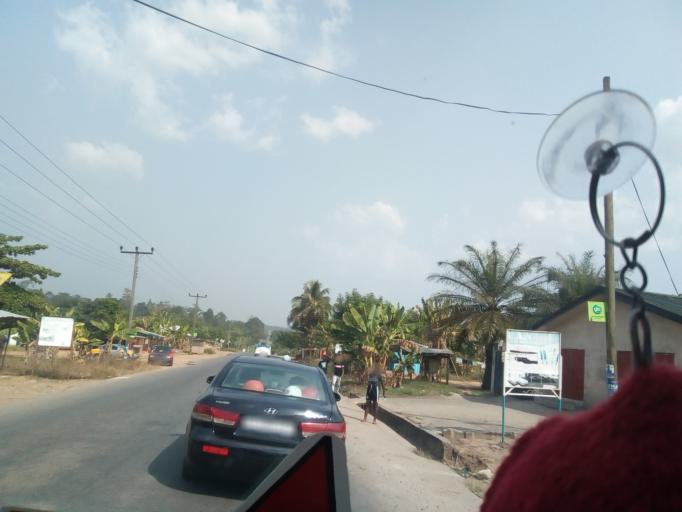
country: GH
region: Eastern
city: Suhum
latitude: 6.0428
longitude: -0.4329
